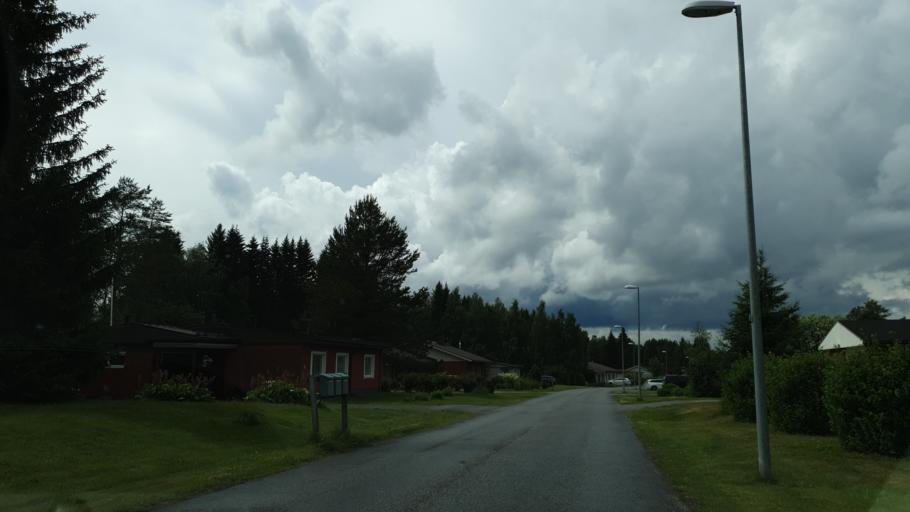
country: FI
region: Kainuu
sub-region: Kehys-Kainuu
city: Kuhmo
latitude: 64.1193
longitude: 29.5148
